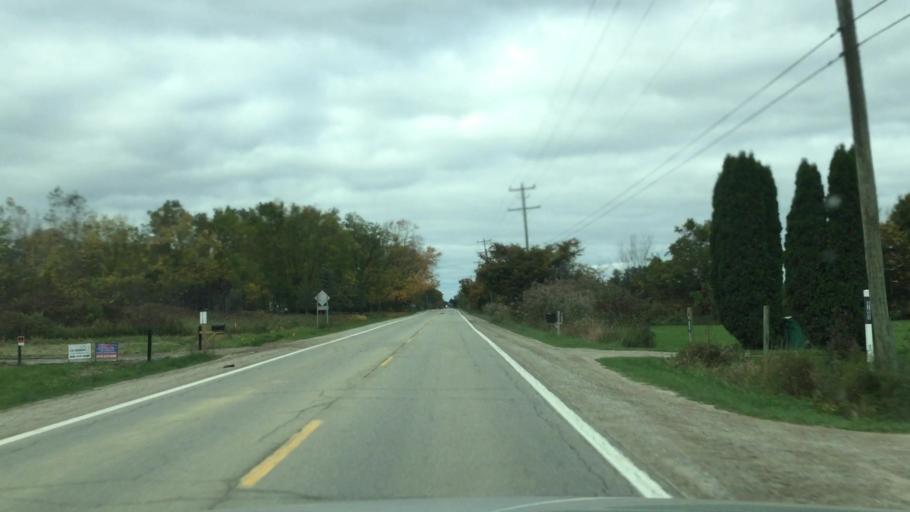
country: US
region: Michigan
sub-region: Macomb County
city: Armada
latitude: 42.8060
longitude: -82.9045
